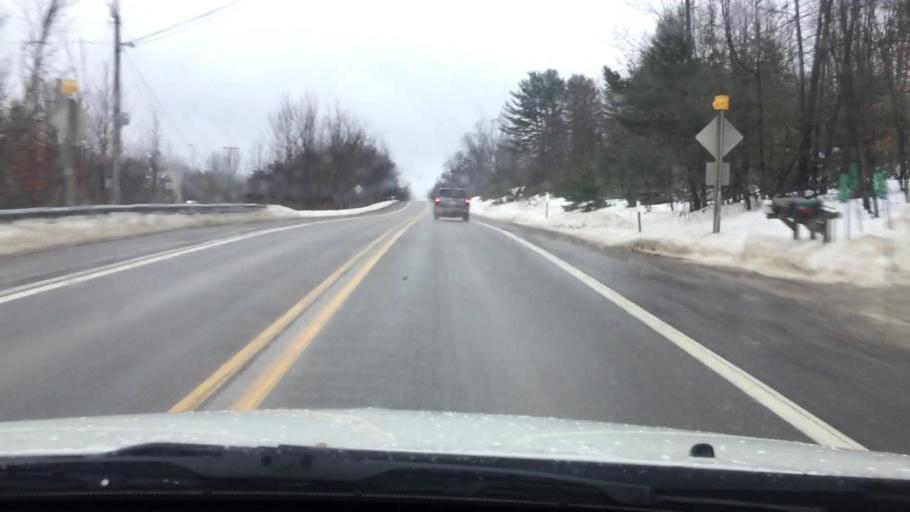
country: US
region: Michigan
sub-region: Charlevoix County
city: East Jordan
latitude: 45.2454
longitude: -85.1809
